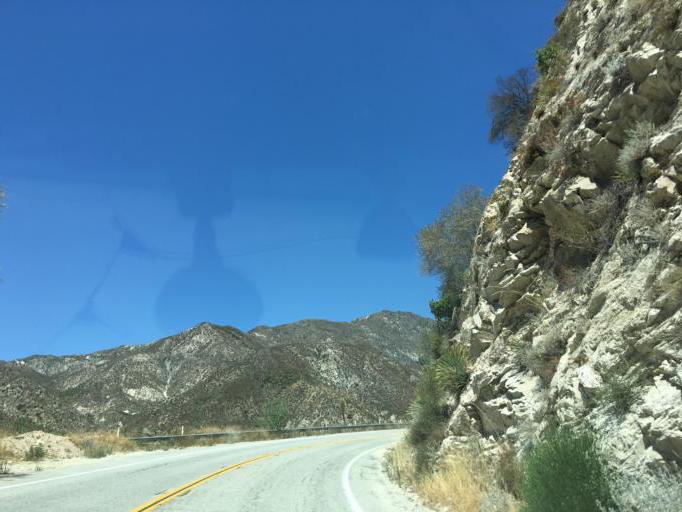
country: US
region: California
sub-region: Los Angeles County
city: La Crescenta-Montrose
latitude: 34.2863
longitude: -118.1913
